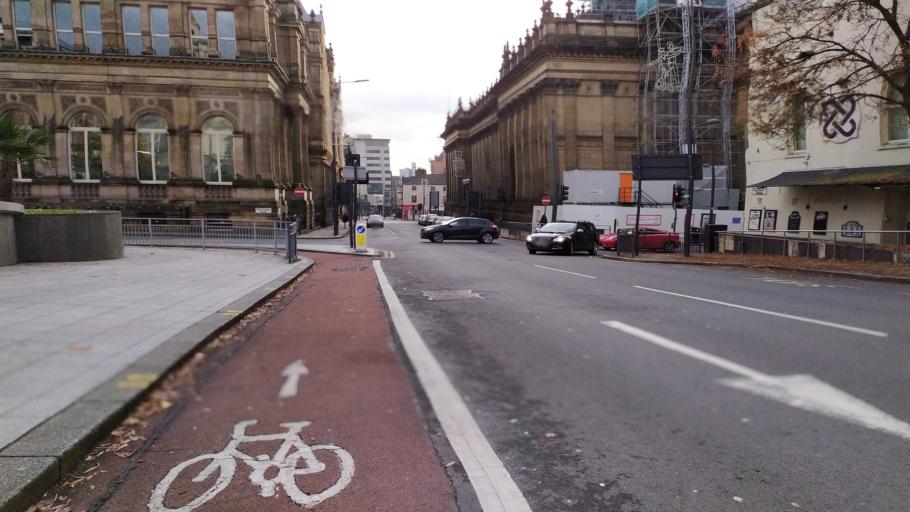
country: GB
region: England
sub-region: City and Borough of Leeds
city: Leeds
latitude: 53.8011
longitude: -1.5490
